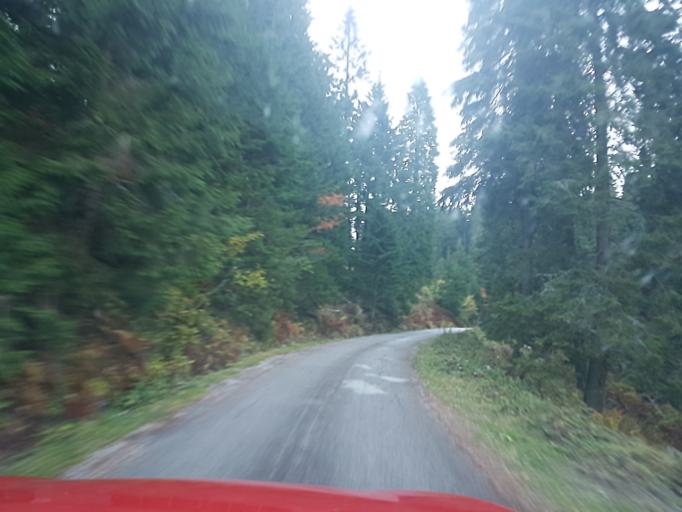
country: SK
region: Zilinsky
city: Ruzomberok
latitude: 48.9964
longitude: 19.2070
